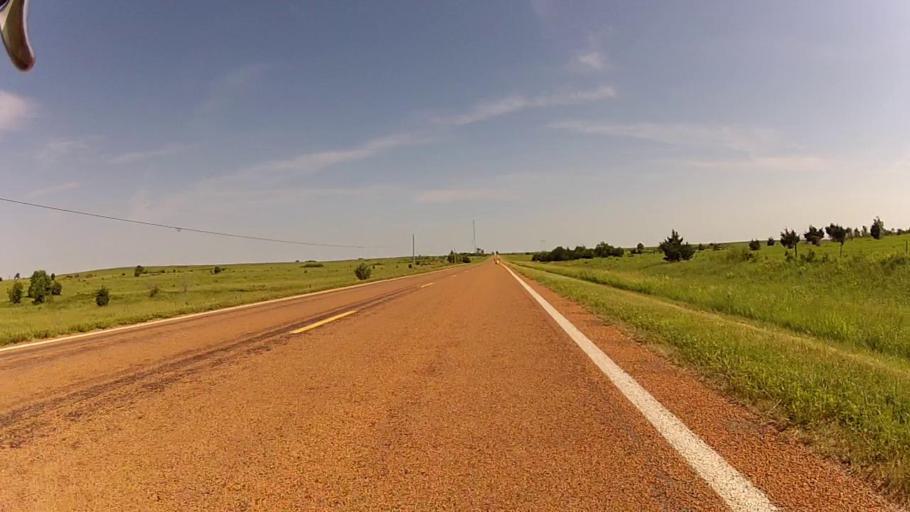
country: US
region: Kansas
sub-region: Cowley County
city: Winfield
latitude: 37.1016
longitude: -96.6436
